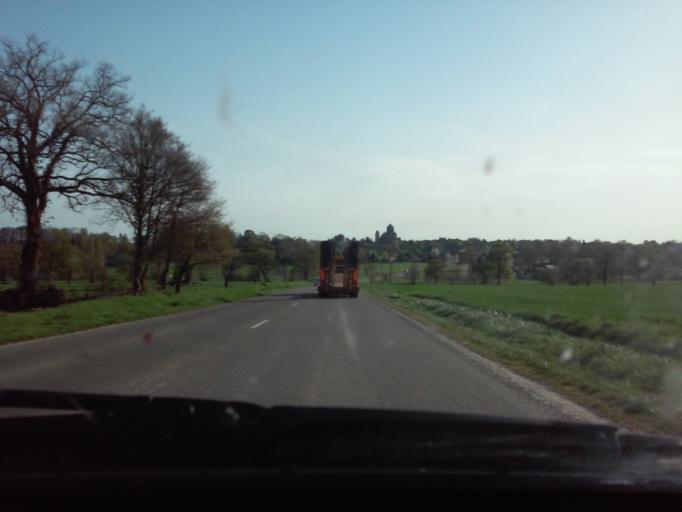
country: FR
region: Brittany
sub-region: Departement d'Ille-et-Vilaine
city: Saint-Aubin-du-Cormier
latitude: 48.2692
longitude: -1.3922
